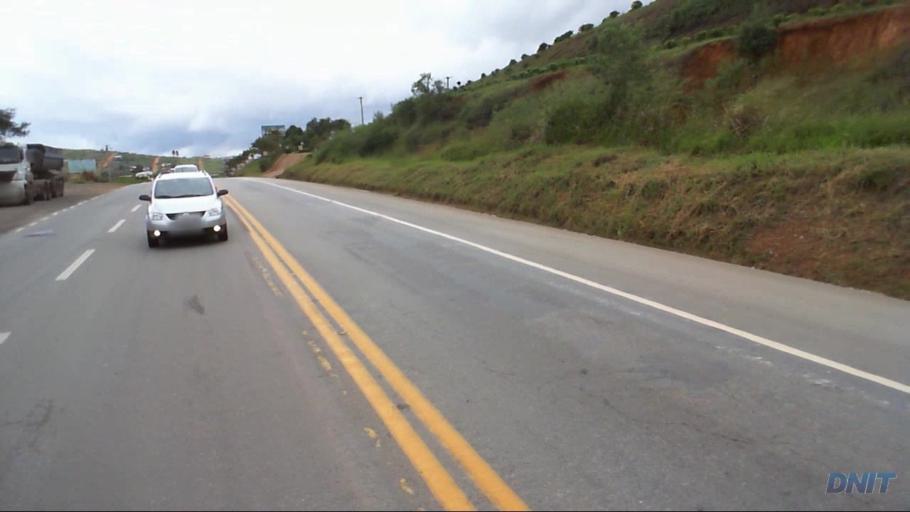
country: BR
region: Minas Gerais
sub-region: Joao Monlevade
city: Joao Monlevade
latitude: -19.8438
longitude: -43.2026
